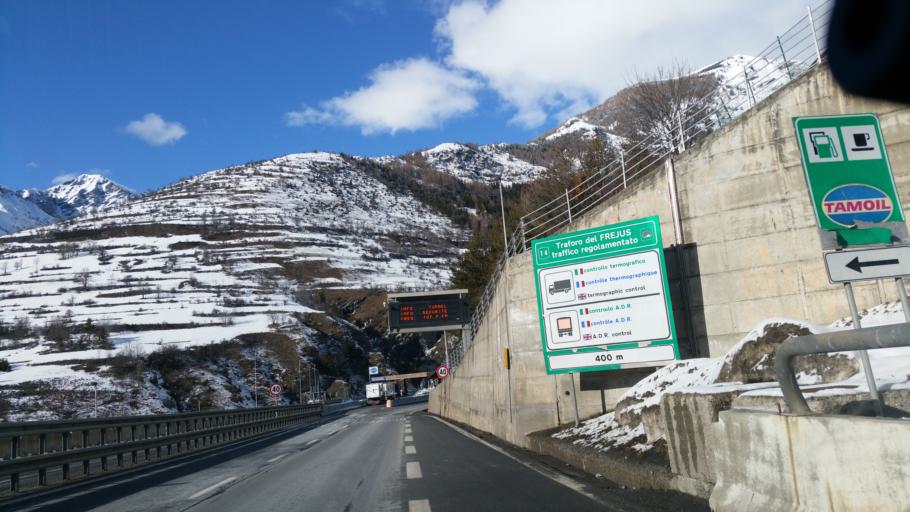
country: IT
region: Piedmont
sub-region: Provincia di Torino
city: Bardonecchia
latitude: 45.0800
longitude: 6.7119
